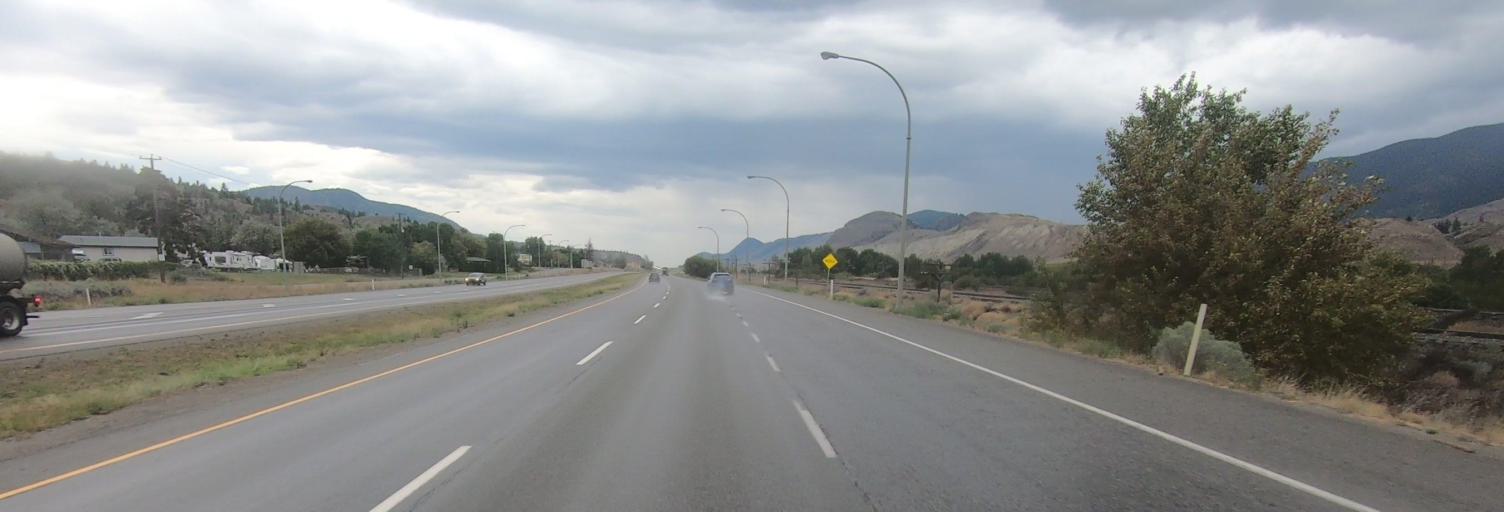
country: CA
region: British Columbia
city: Kamloops
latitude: 50.6547
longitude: -120.0723
